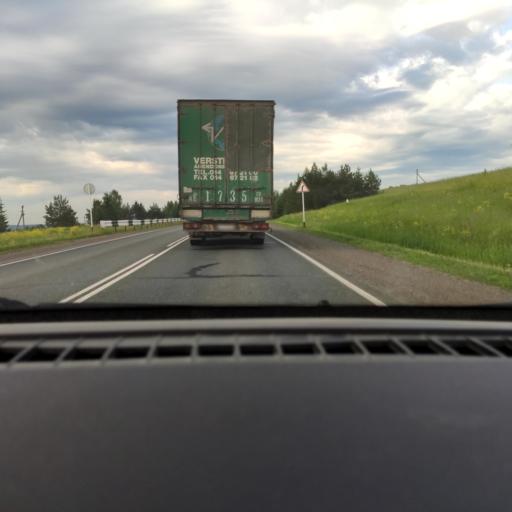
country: RU
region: Perm
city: Chastyye
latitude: 57.3787
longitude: 54.4364
